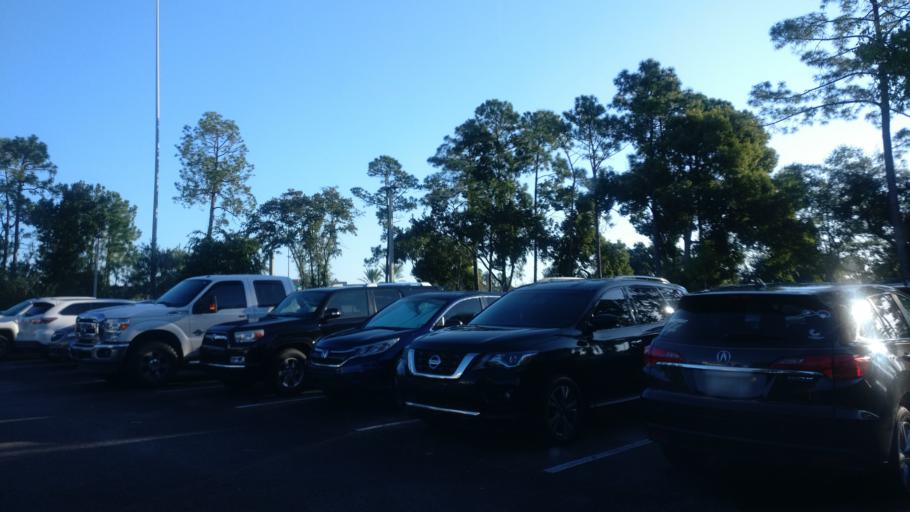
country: US
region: Florida
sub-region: Duval County
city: Jacksonville
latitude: 30.2504
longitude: -81.5852
